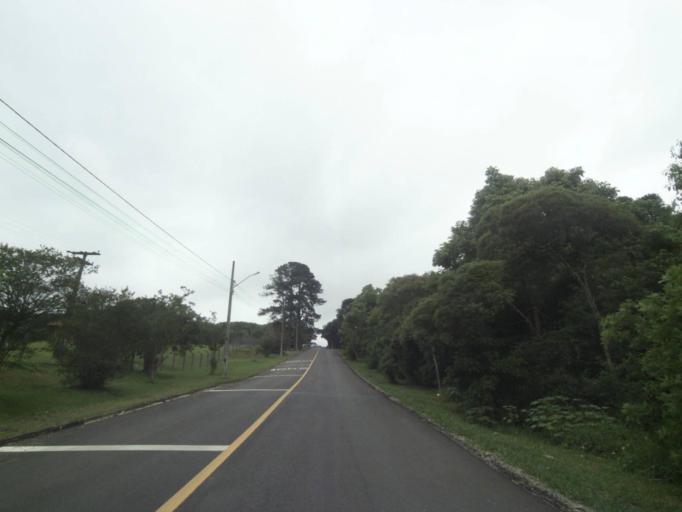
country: BR
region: Parana
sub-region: Curitiba
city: Curitiba
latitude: -25.4915
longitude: -49.3534
